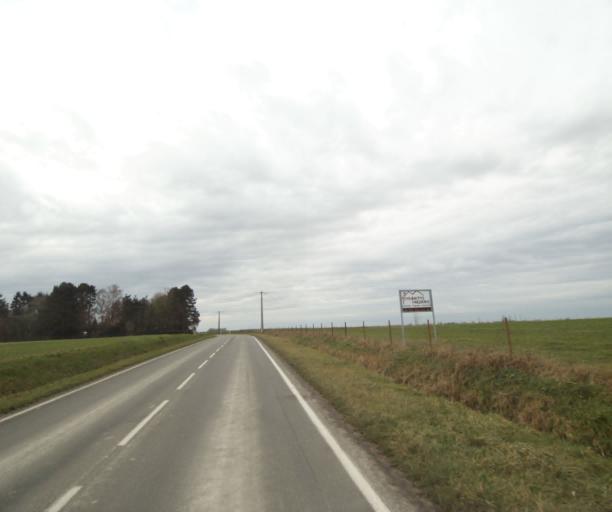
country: FR
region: Nord-Pas-de-Calais
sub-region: Departement du Nord
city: Sebourg
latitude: 50.3604
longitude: 3.6441
